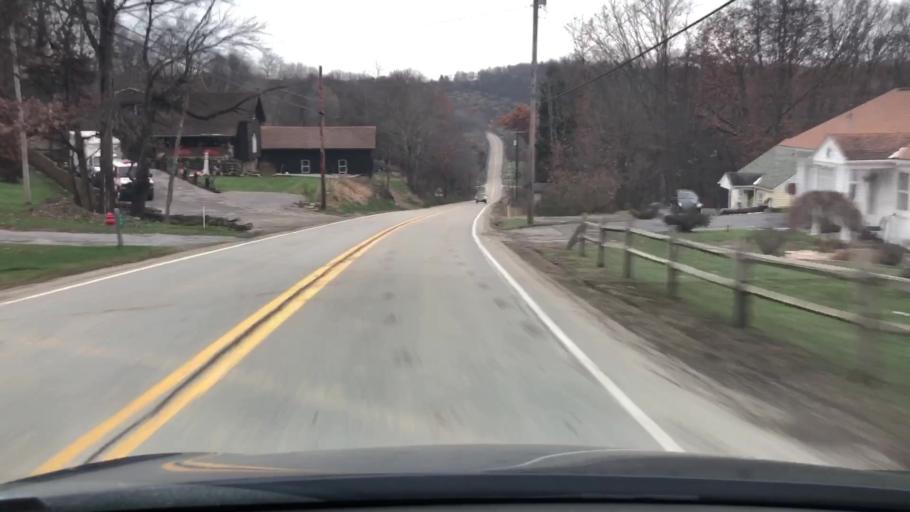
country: US
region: Pennsylvania
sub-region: Armstrong County
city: Kittanning
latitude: 40.8491
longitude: -79.4591
